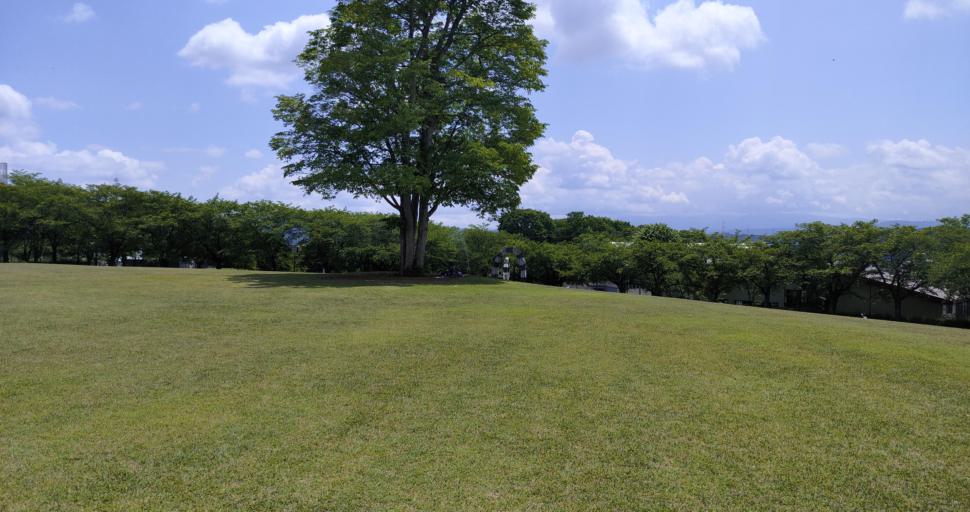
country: JP
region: Nagano
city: Ueda
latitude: 36.3632
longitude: 138.3496
